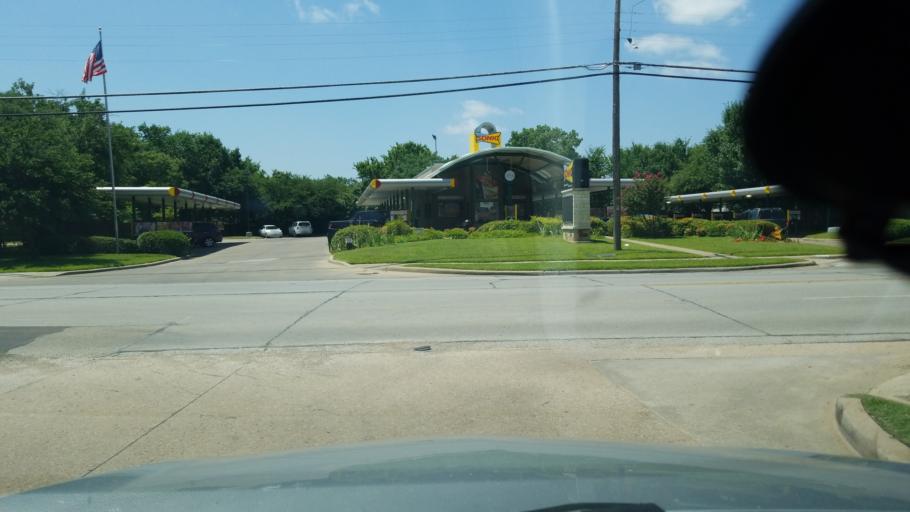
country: US
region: Texas
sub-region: Dallas County
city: Irving
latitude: 32.8225
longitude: -96.9624
